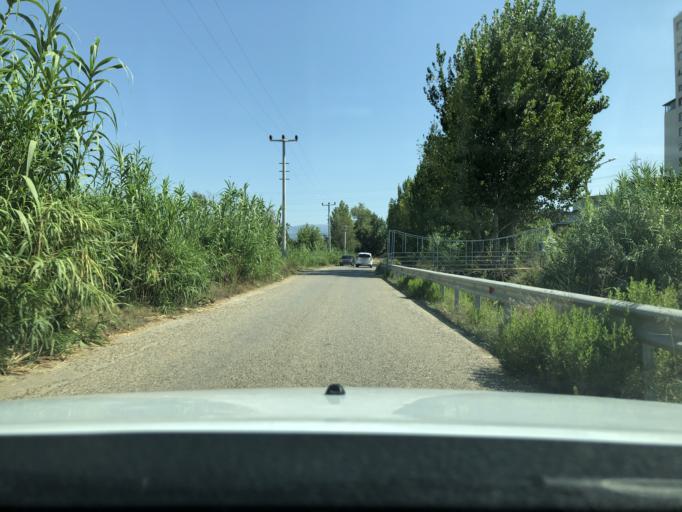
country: TR
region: Antalya
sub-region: Manavgat
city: Manavgat
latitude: 36.7972
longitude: 31.4650
